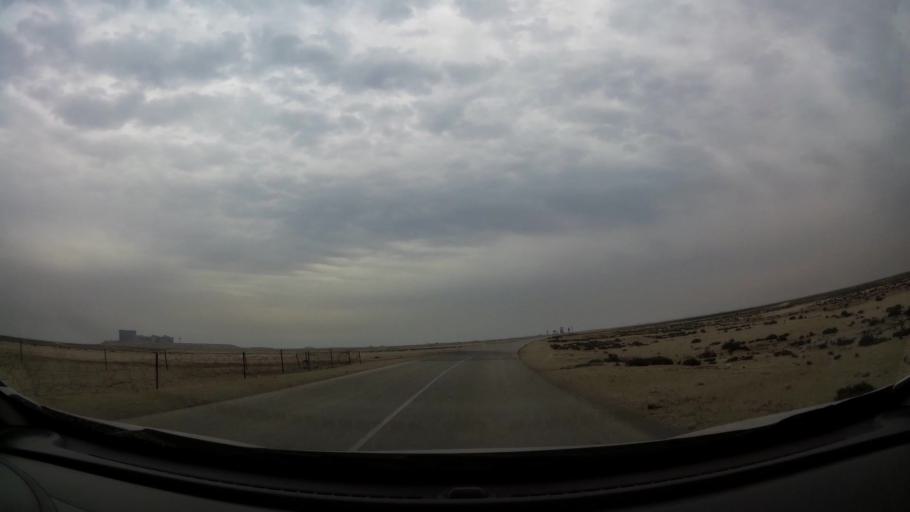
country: BH
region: Central Governorate
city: Dar Kulayb
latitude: 25.8760
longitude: 50.5978
